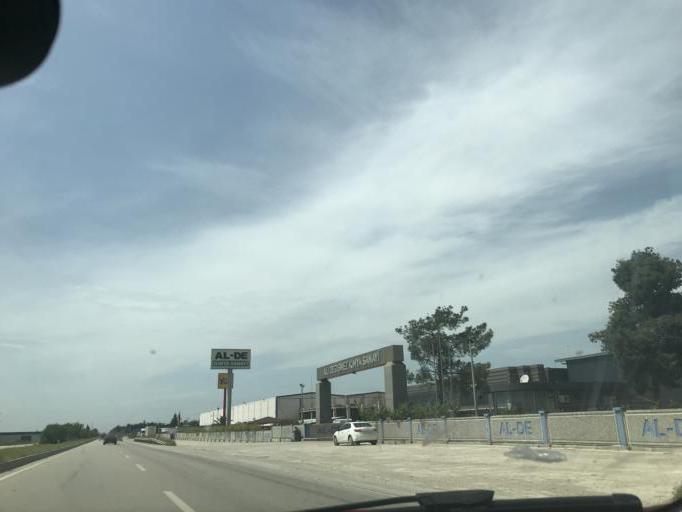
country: TR
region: Adana
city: Yakapinar
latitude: 36.9705
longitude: 35.5292
